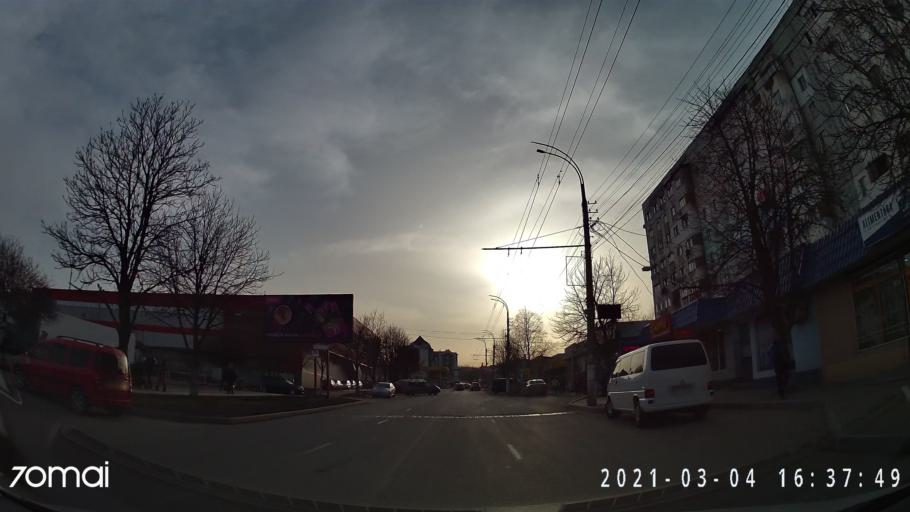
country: MD
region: Balti
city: Balti
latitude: 47.7827
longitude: 27.8919
